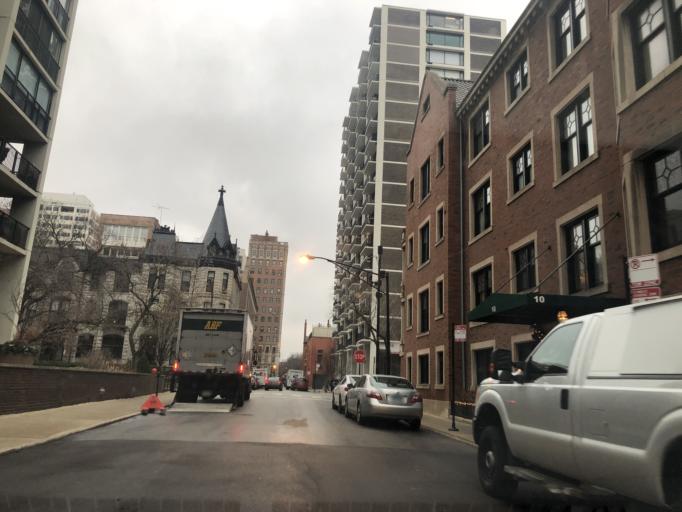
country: US
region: Illinois
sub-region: Cook County
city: Chicago
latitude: 41.9078
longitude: -87.6281
